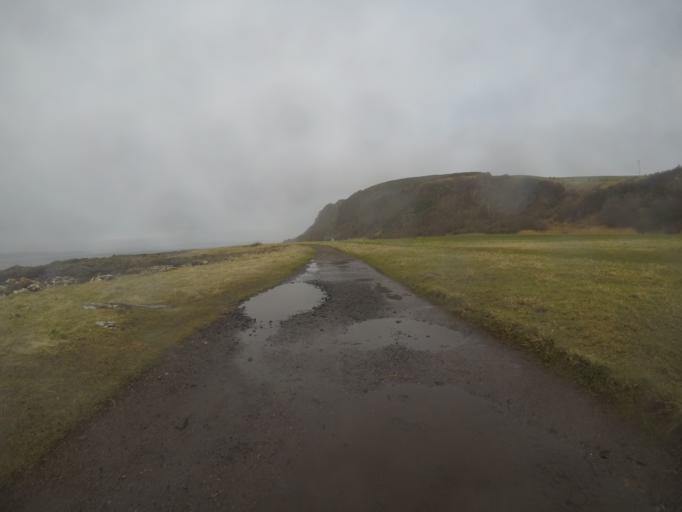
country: GB
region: Scotland
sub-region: North Ayrshire
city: Millport
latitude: 55.7032
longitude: -4.9041
